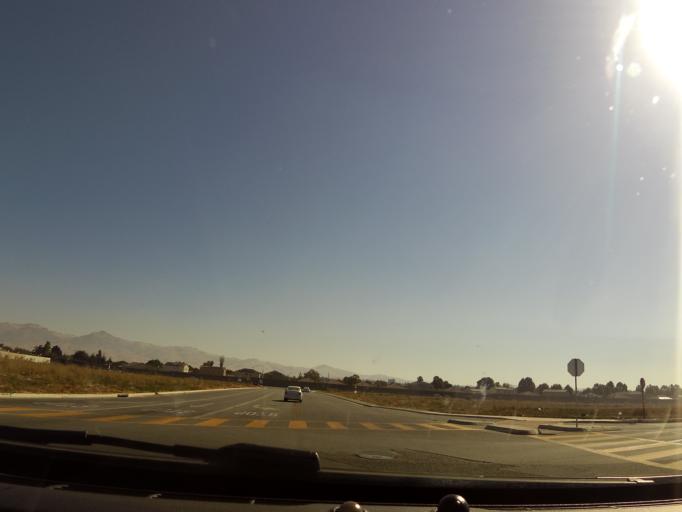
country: US
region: California
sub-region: San Benito County
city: Hollister
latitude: 36.8434
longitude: -121.3936
